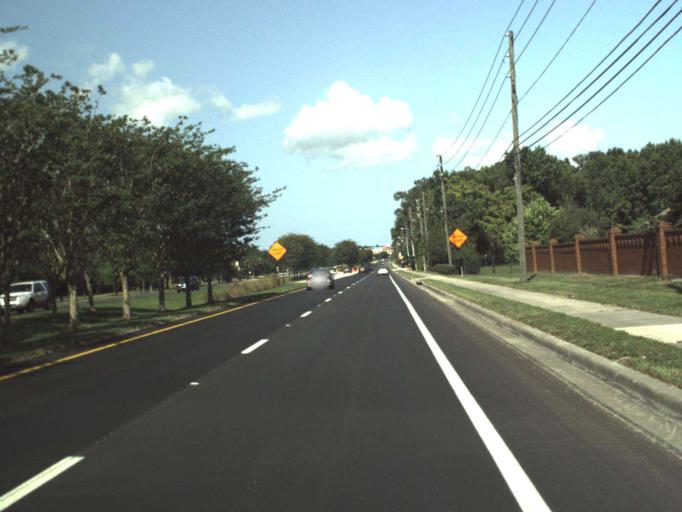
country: US
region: Florida
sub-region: Seminole County
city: Winter Springs
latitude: 28.7044
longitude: -81.2837
